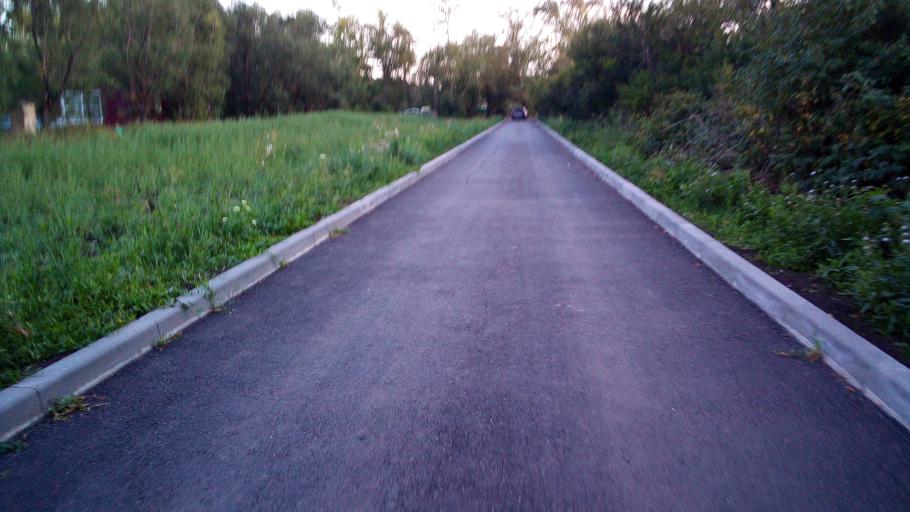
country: RU
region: Chelyabinsk
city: Potanino
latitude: 55.2919
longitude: 61.5116
